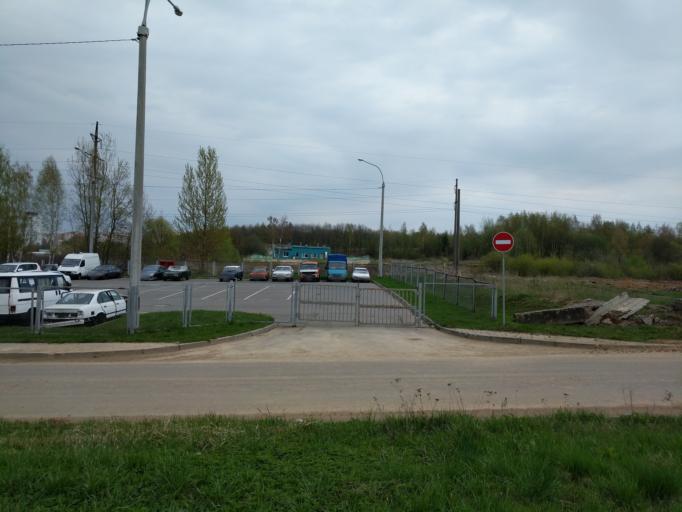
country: BY
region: Minsk
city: Novoye Medvezhino
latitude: 53.8914
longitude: 27.4625
